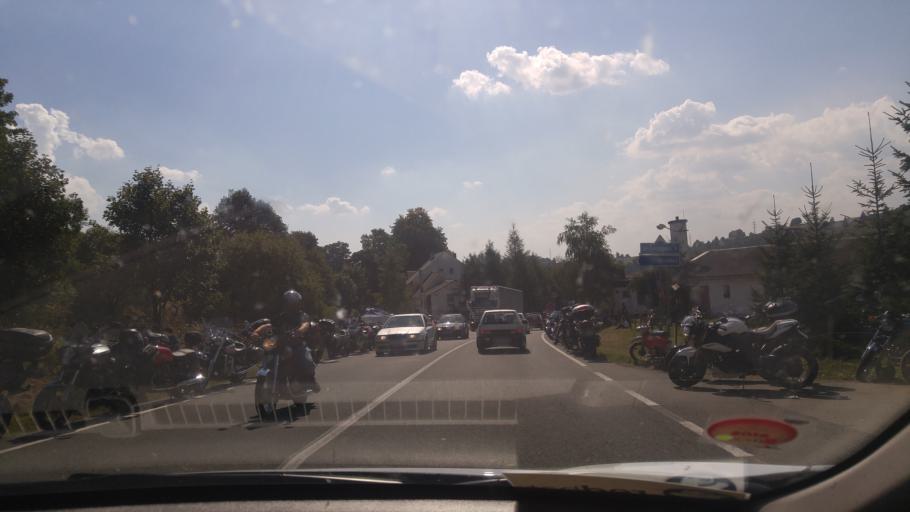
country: CZ
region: Olomoucky
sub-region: Okres Sumperk
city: Stare Mesto
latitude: 50.1584
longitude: 17.0157
